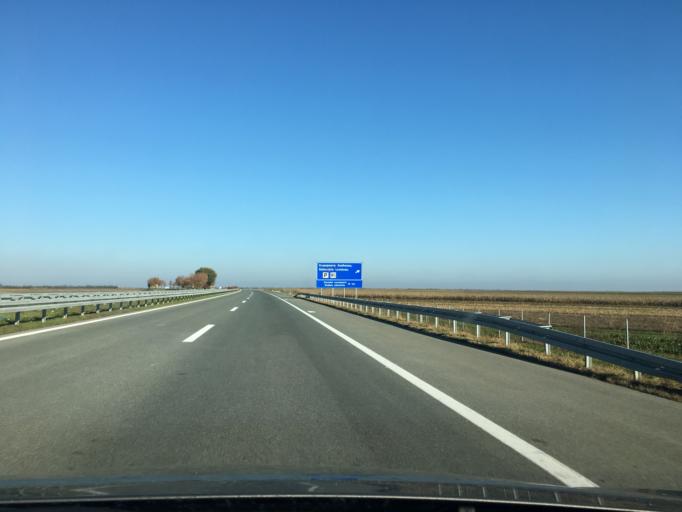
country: RS
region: Autonomna Pokrajina Vojvodina
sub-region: Severnobacki Okrug
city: Mali Igos
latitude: 45.6715
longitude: 19.7287
